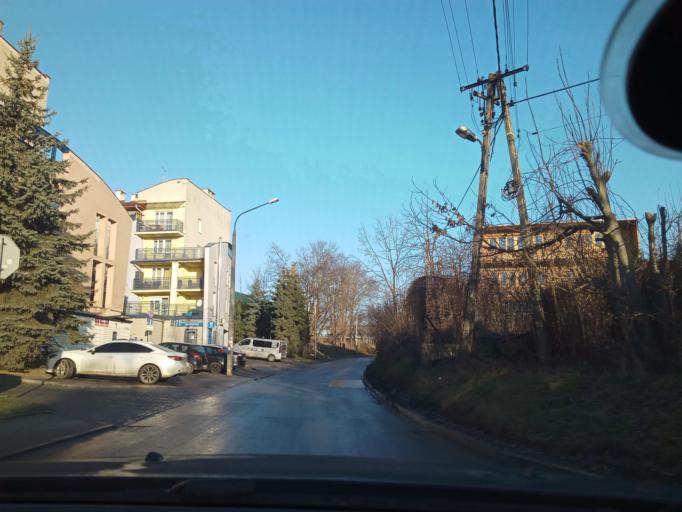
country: PL
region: Lesser Poland Voivodeship
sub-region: Powiat krakowski
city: Michalowice
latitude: 50.0983
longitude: 20.0253
